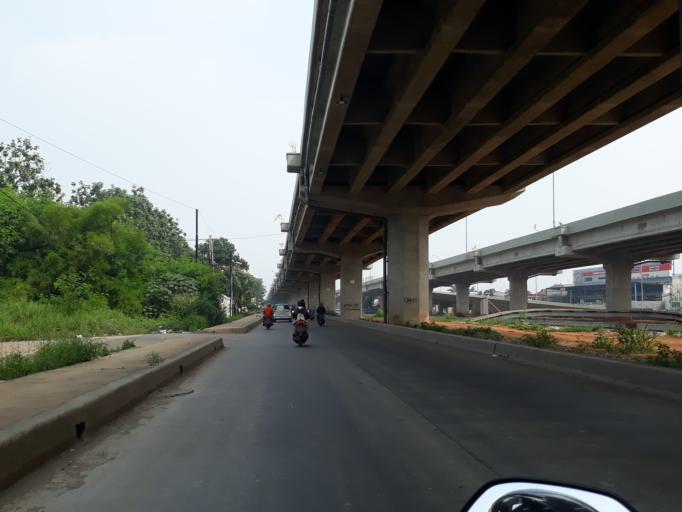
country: ID
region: West Java
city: Bekasi
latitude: -6.2491
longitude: 106.9323
